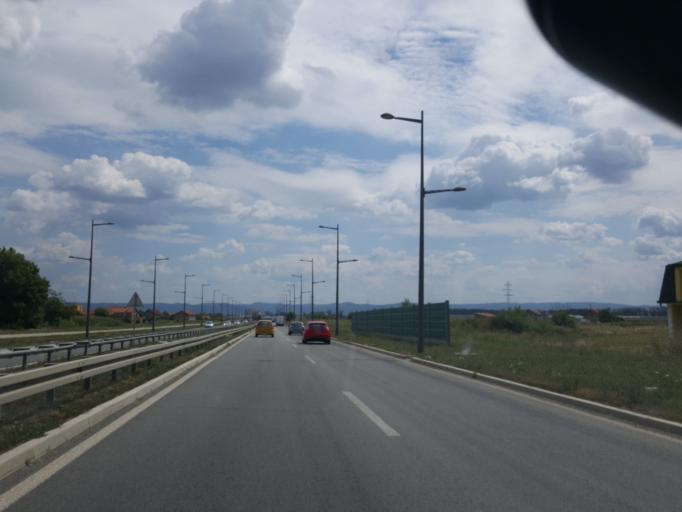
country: RS
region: Autonomna Pokrajina Vojvodina
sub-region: Juznobacki Okrug
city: Novi Sad
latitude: 45.2998
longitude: 19.8078
